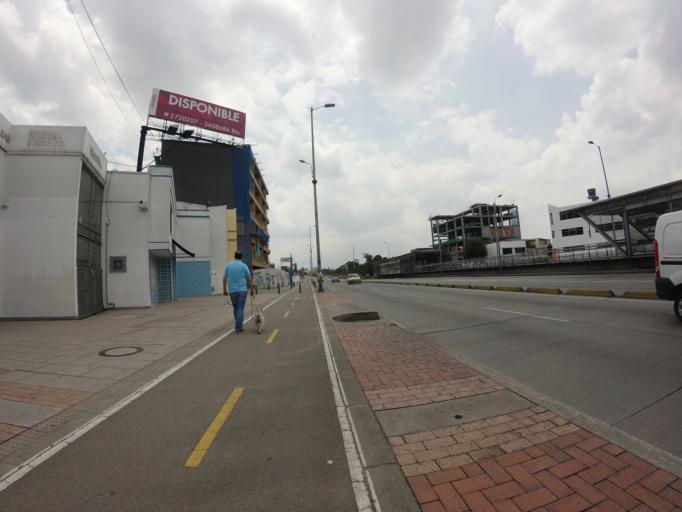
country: CO
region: Bogota D.C.
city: Barrio San Luis
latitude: 4.6804
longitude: -74.0645
